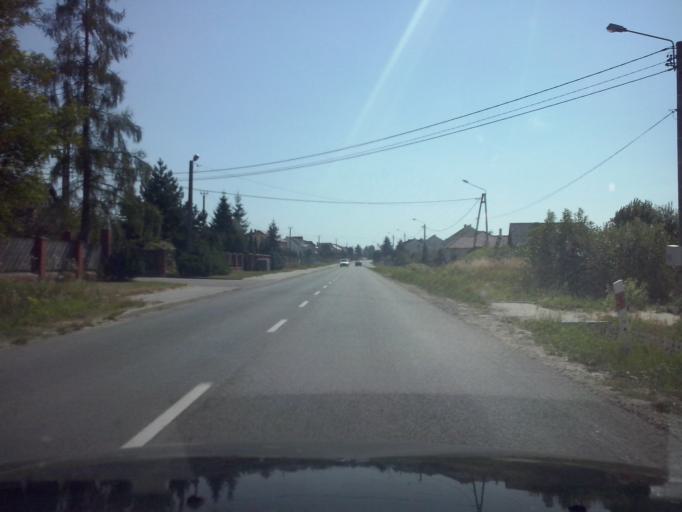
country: PL
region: Swietokrzyskie
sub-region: Powiat kielecki
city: Daleszyce
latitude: 50.8077
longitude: 20.7907
